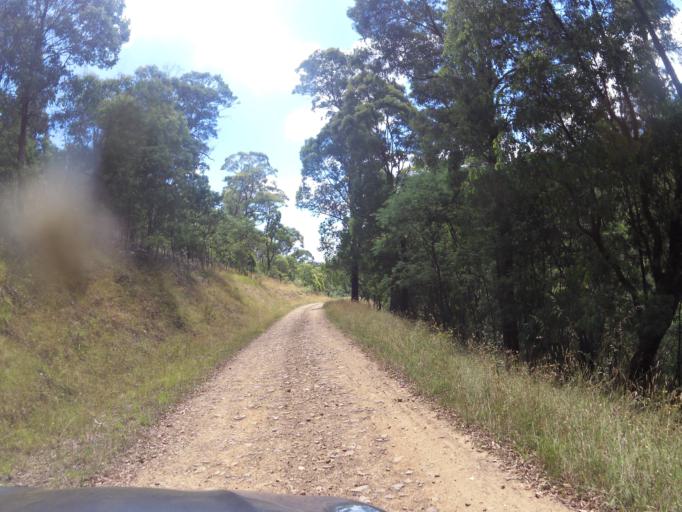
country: AU
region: Victoria
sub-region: Alpine
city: Mount Beauty
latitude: -36.7907
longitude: 147.0826
